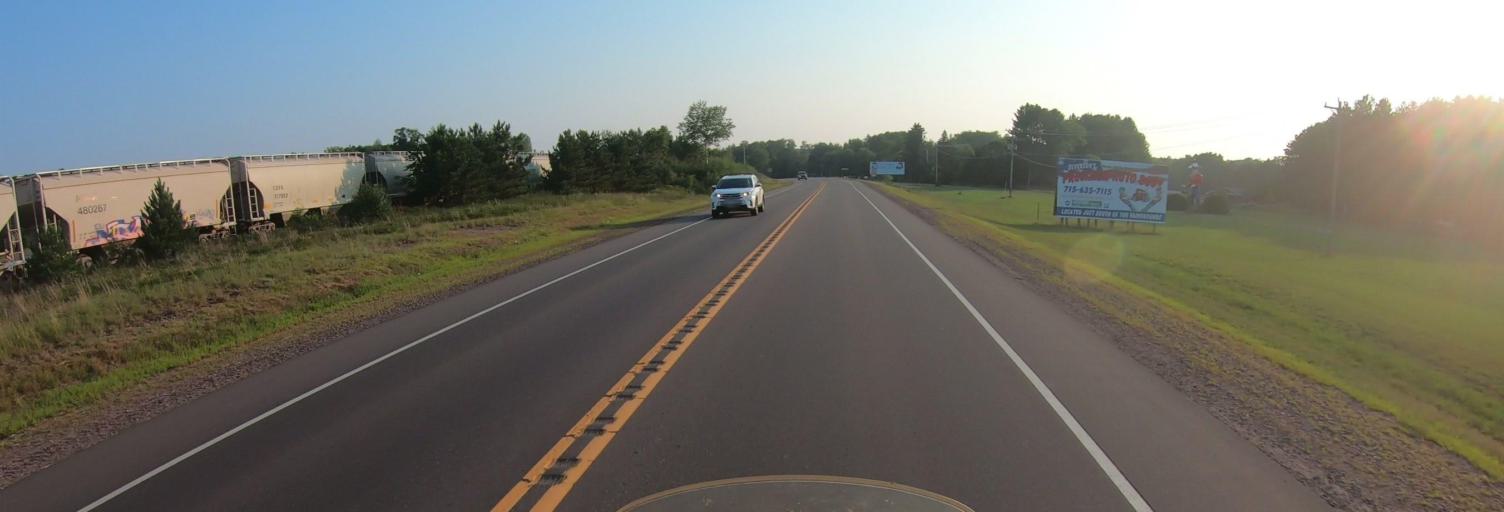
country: US
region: Wisconsin
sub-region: Washburn County
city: Spooner
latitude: 45.8427
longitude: -91.8759
